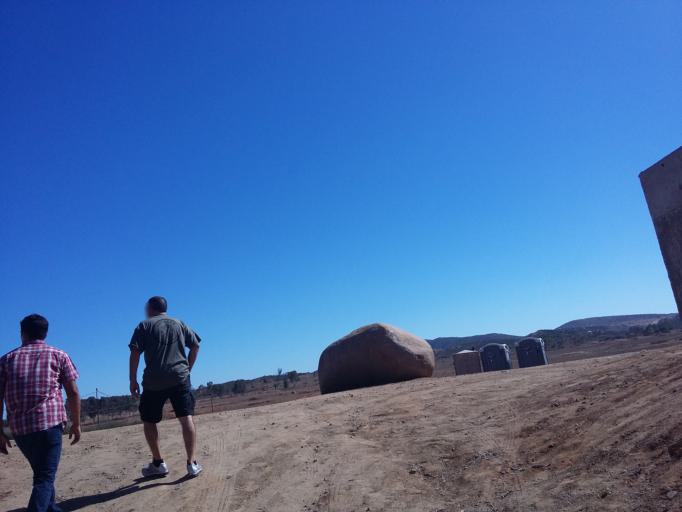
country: MX
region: Baja California
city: El Sauzal
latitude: 32.0022
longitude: -116.6754
